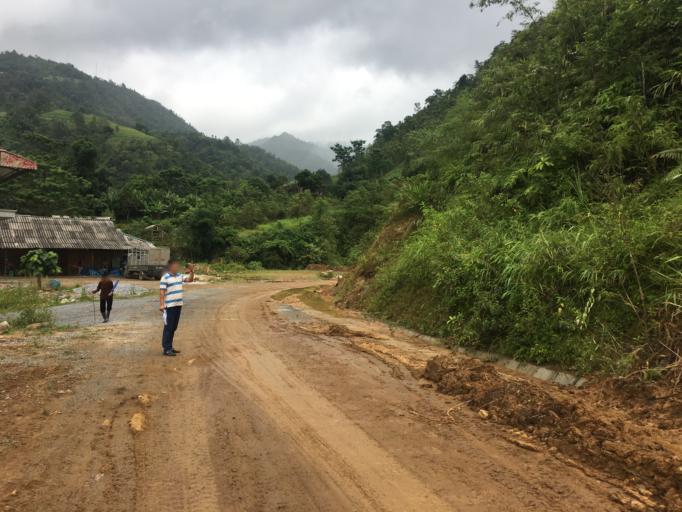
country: VN
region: Ha Giang
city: Thi Tran Tam Son
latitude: 22.9940
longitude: 105.0752
